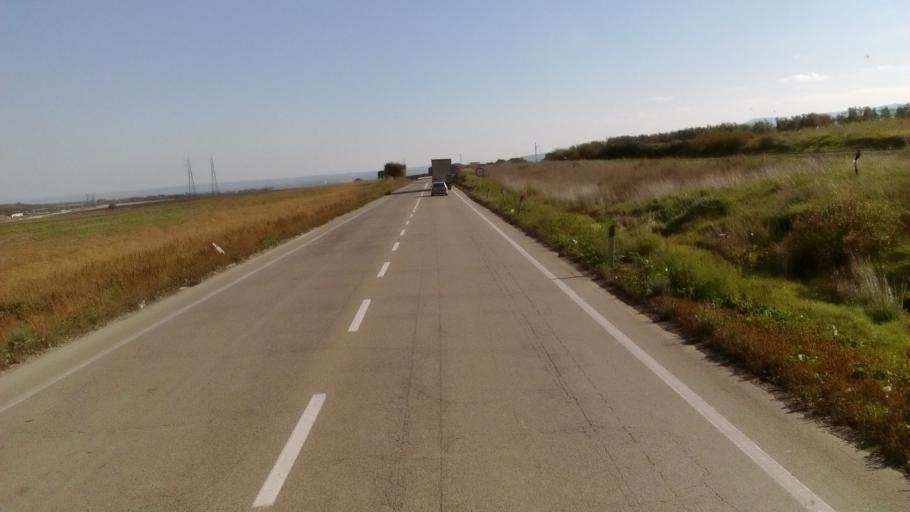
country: IT
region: Apulia
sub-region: Provincia di Foggia
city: Candela
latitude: 41.1196
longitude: 15.5737
